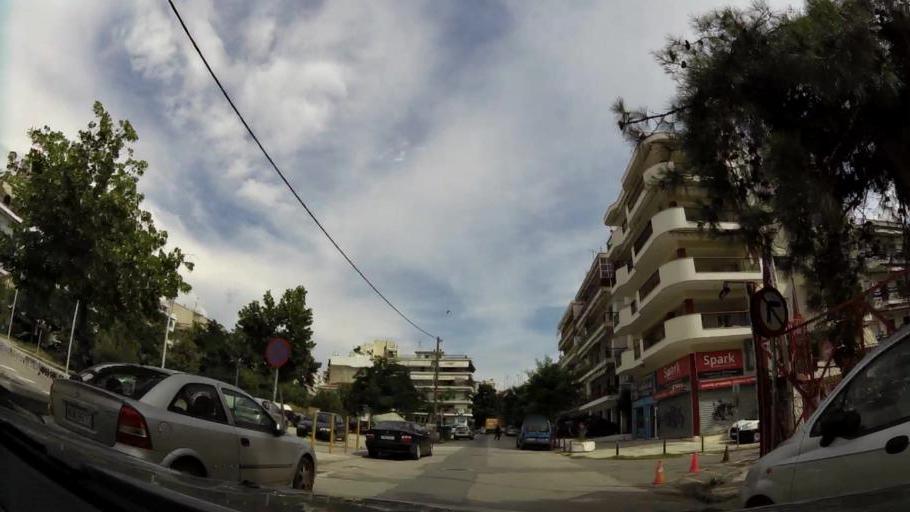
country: GR
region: Central Macedonia
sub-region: Nomos Thessalonikis
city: Kalamaria
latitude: 40.5806
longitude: 22.9488
